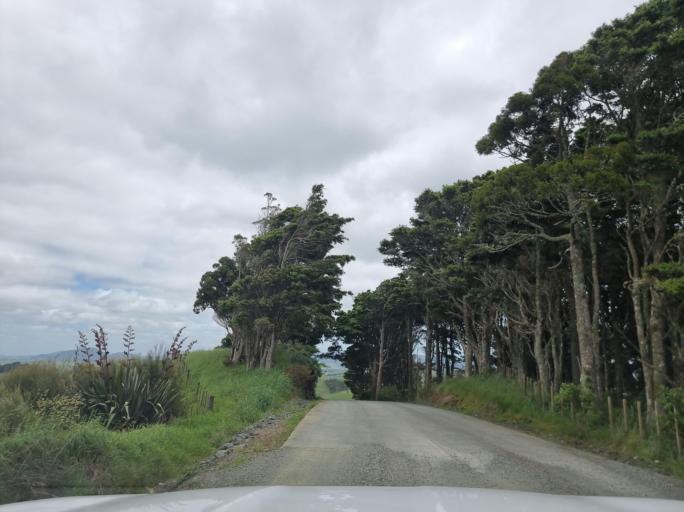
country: NZ
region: Auckland
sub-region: Auckland
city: Wellsford
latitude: -36.1663
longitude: 174.5531
